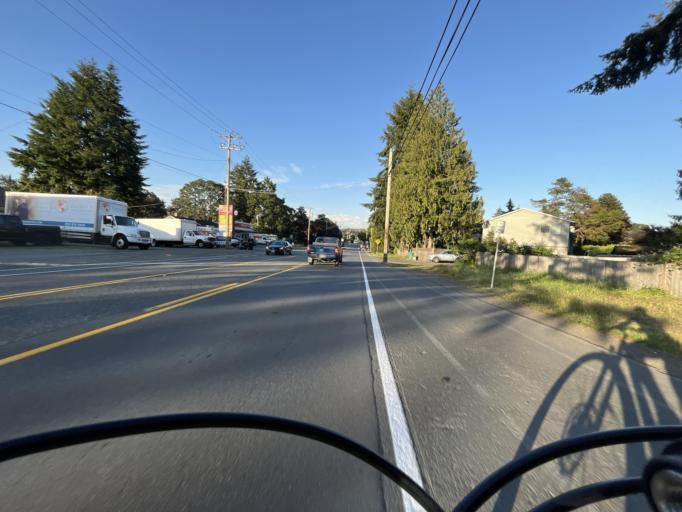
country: CA
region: British Columbia
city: Langford
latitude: 48.4502
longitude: -123.5110
